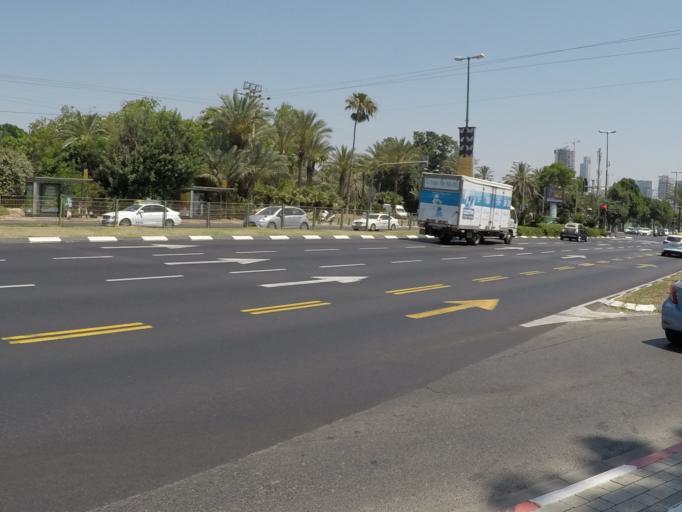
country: IL
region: Tel Aviv
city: Tel Aviv
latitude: 32.1036
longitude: 34.7924
